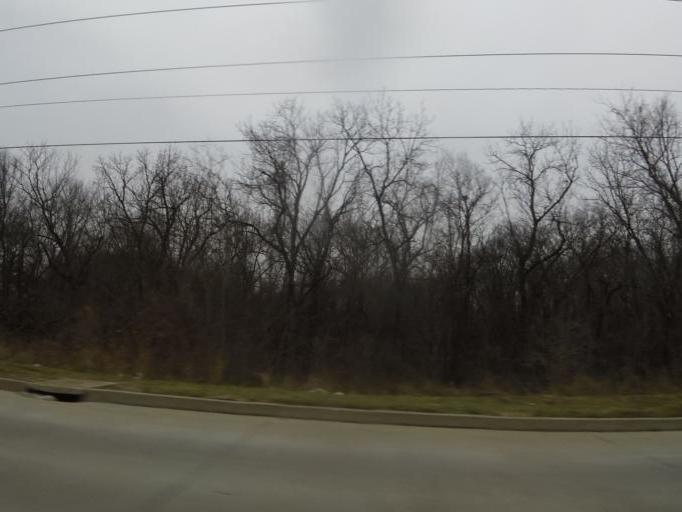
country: US
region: Missouri
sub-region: Marion County
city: Hannibal
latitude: 39.7209
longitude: -91.4009
